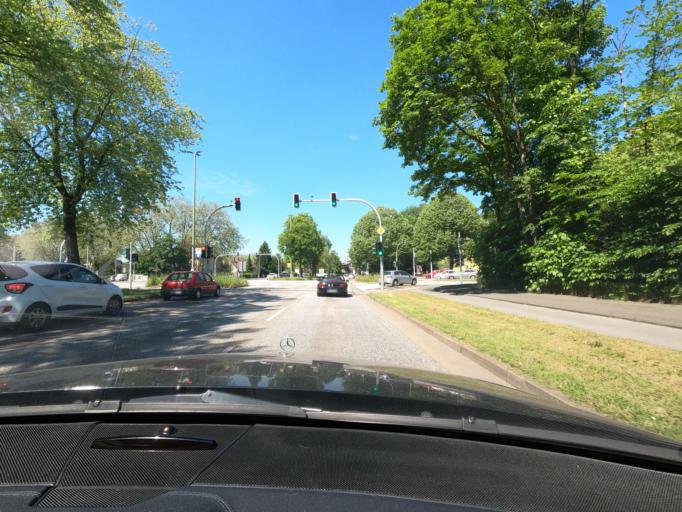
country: DE
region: North Rhine-Westphalia
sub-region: Regierungsbezirk Dusseldorf
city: Hochfeld
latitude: 51.3923
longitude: 6.7592
